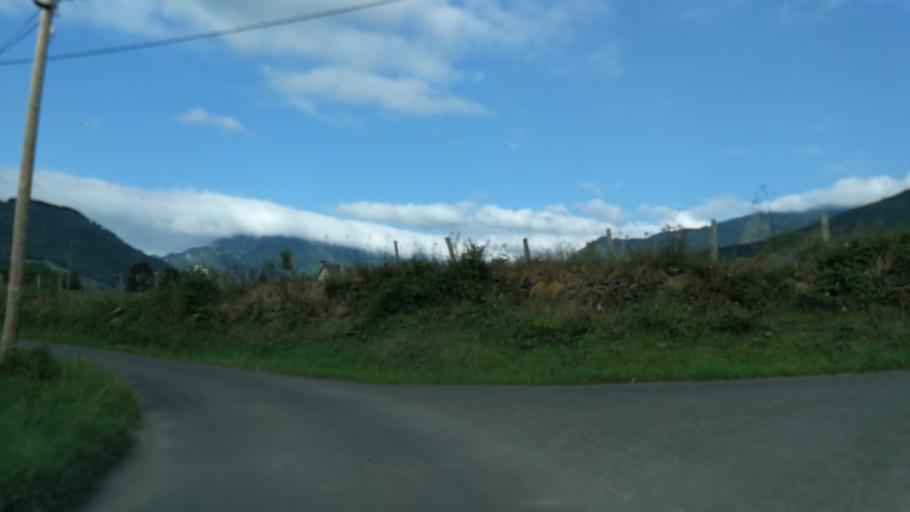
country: FR
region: Aquitaine
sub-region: Departement des Pyrenees-Atlantiques
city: Arette
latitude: 42.9213
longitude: -0.6552
